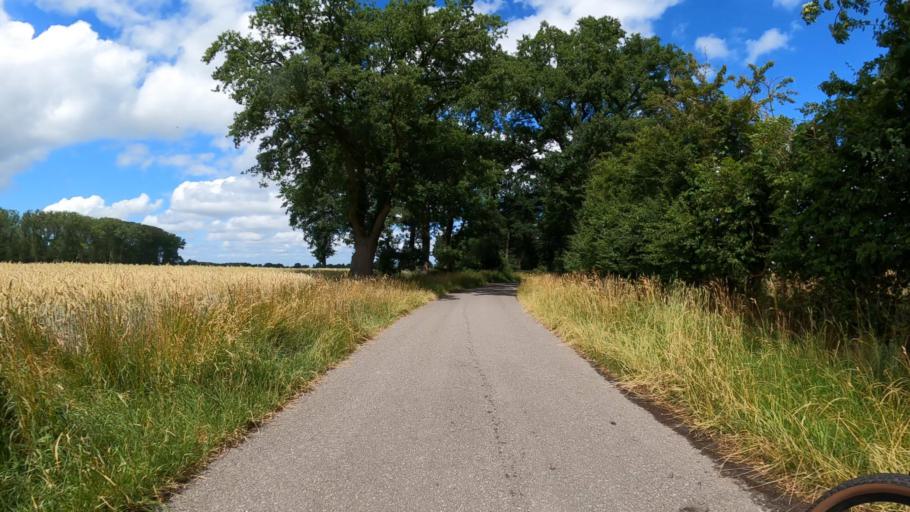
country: DE
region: Lower Saxony
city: Neu Wulmstorf
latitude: 53.4535
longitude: 9.7581
